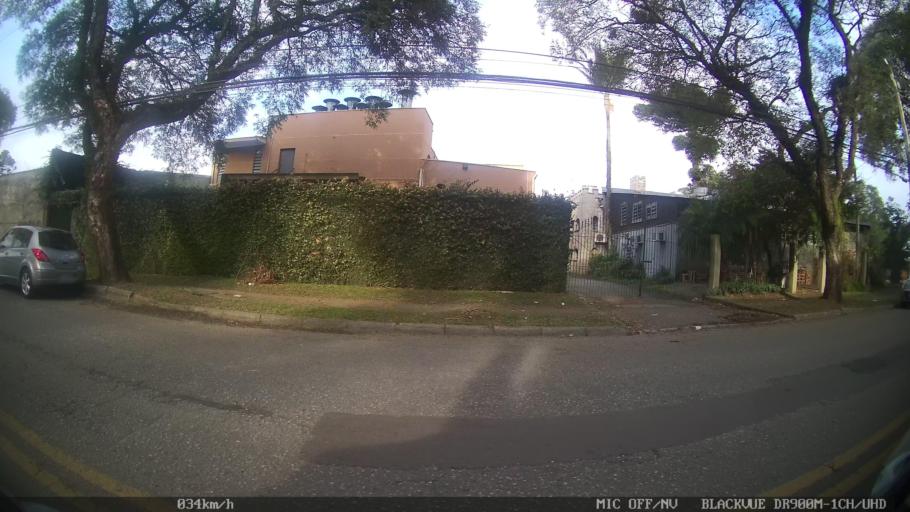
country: BR
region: Parana
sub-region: Curitiba
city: Curitiba
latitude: -25.3992
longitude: -49.3356
